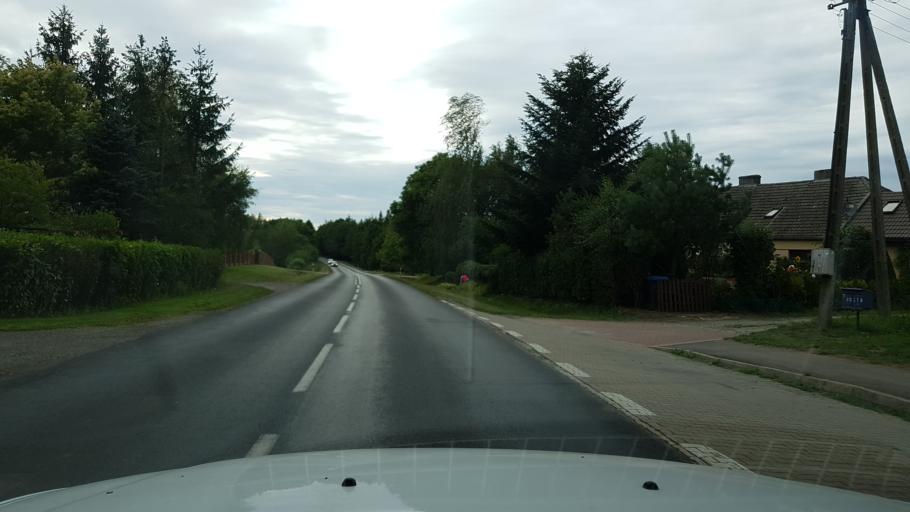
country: PL
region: West Pomeranian Voivodeship
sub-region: Powiat kolobrzeski
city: Dygowo
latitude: 54.1388
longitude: 15.7047
